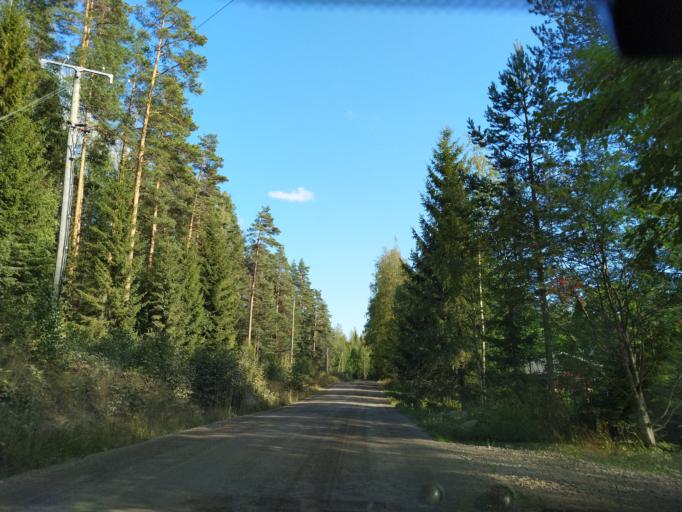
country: FI
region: Central Finland
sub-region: Jaemsae
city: Kuhmoinen
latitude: 61.7099
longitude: 24.9109
